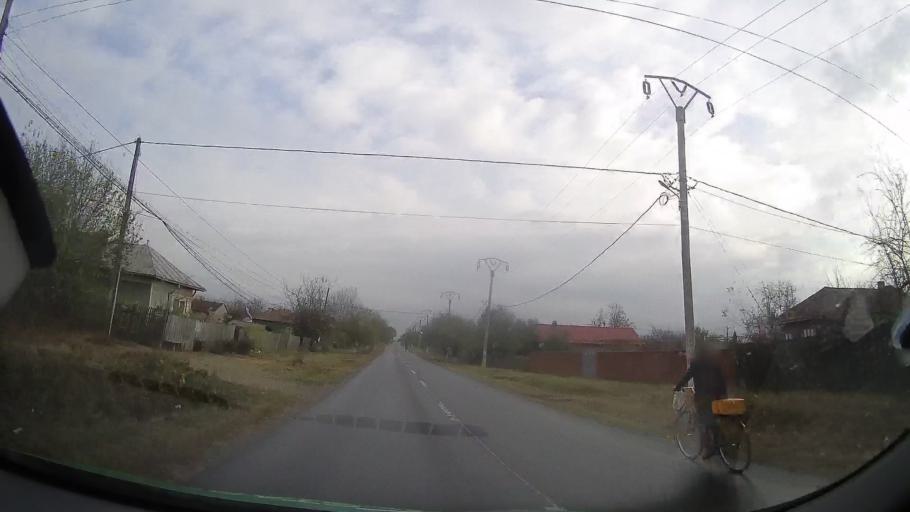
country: RO
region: Ialomita
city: Brazii
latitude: 44.7594
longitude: 26.3652
